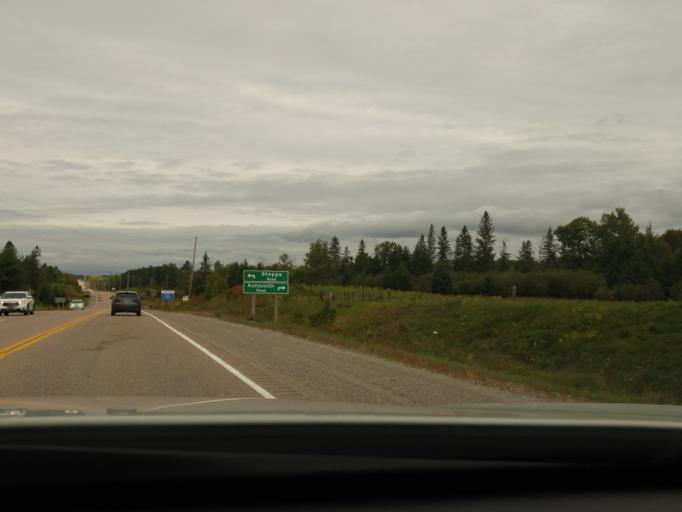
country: CA
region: Ontario
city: Renfrew
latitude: 45.6039
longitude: -76.8504
